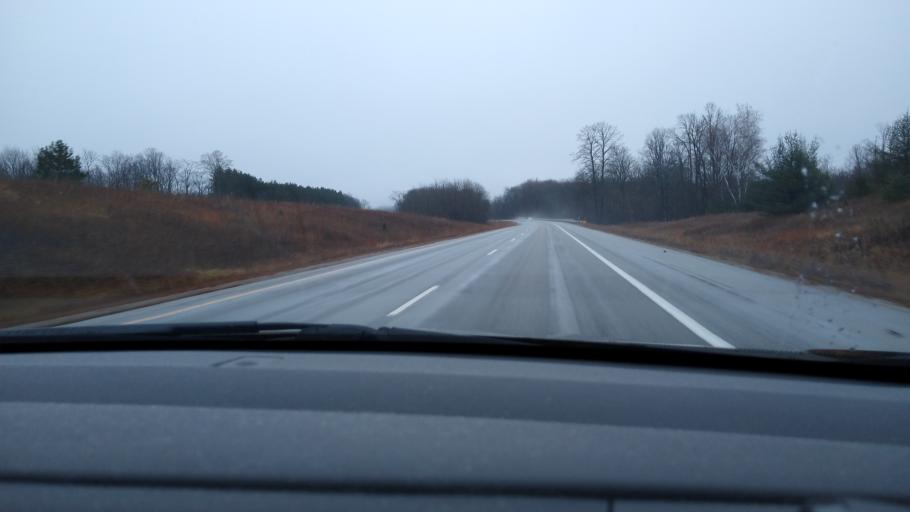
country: US
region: Michigan
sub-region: Cheboygan County
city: Indian River
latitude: 45.3294
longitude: -84.6051
